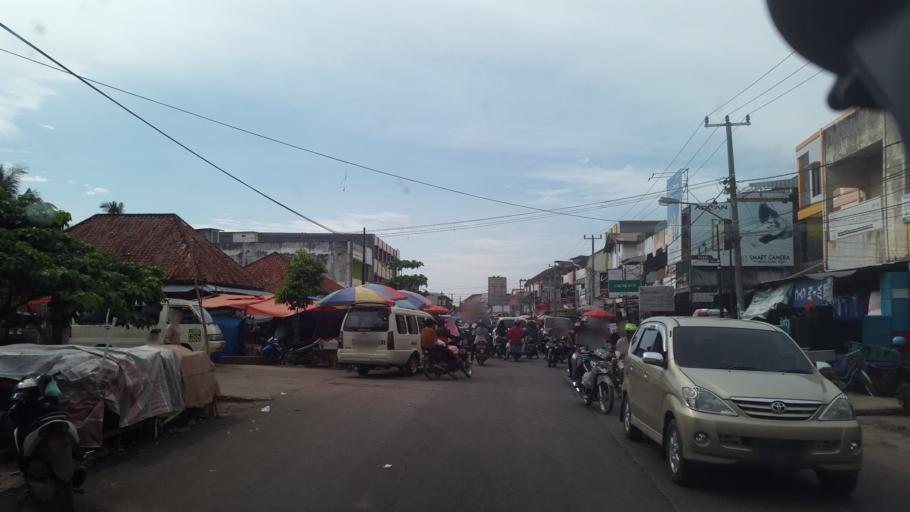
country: ID
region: South Sumatra
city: Plaju
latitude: -2.9972
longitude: 104.8151
